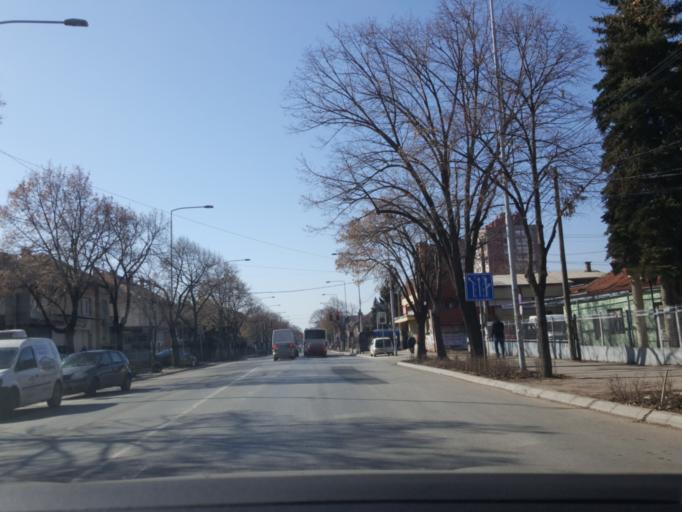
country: RS
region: Central Serbia
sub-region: Nisavski Okrug
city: Nis
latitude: 43.3295
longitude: 21.9265
